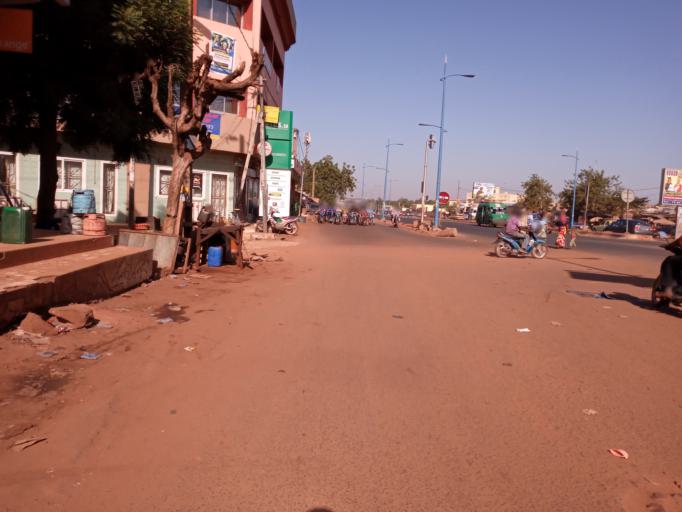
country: ML
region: Bamako
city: Bamako
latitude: 12.6008
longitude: -7.9649
